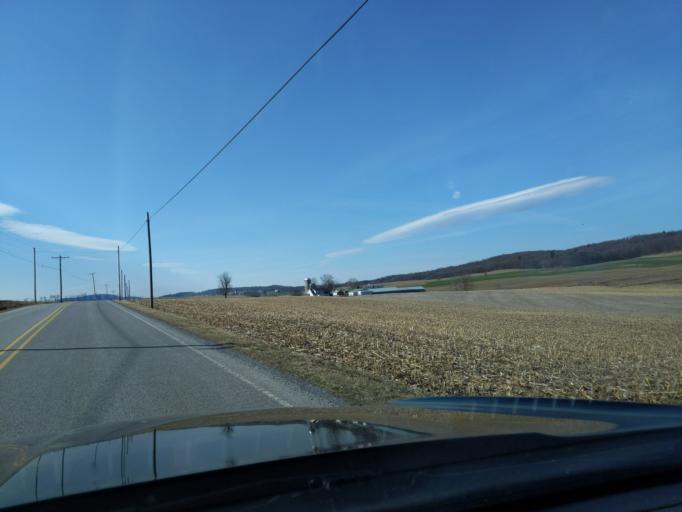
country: US
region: Pennsylvania
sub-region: Blair County
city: Martinsburg
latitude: 40.3372
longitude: -78.2624
